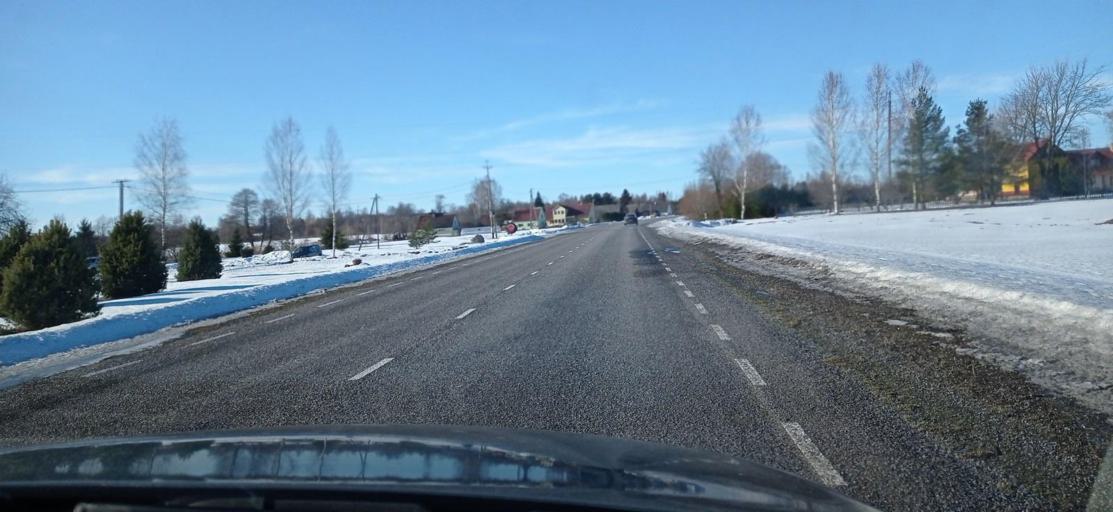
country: EE
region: Tartu
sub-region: Alatskivi vald
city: Kallaste
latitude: 58.5214
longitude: 27.0940
